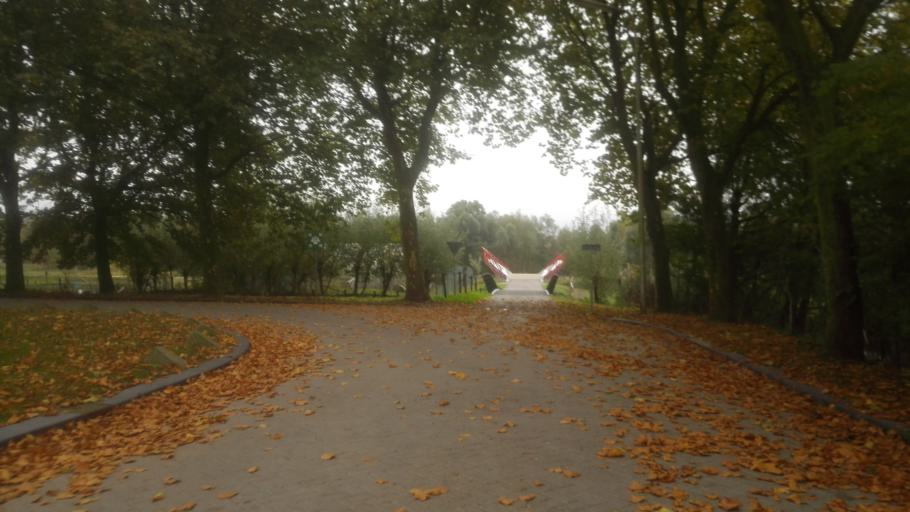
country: NL
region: South Holland
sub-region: Gemeente Delft
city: Delft
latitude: 51.9851
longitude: 4.3873
